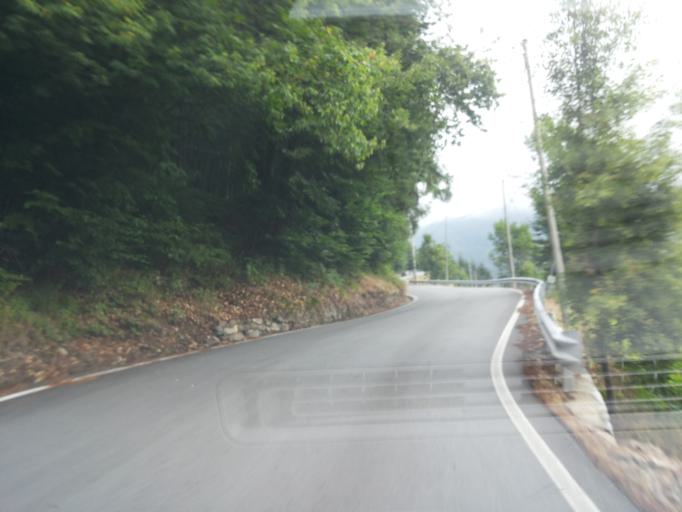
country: IT
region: Piedmont
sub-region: Provincia di Biella
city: Pollone
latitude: 45.6136
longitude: 7.9863
